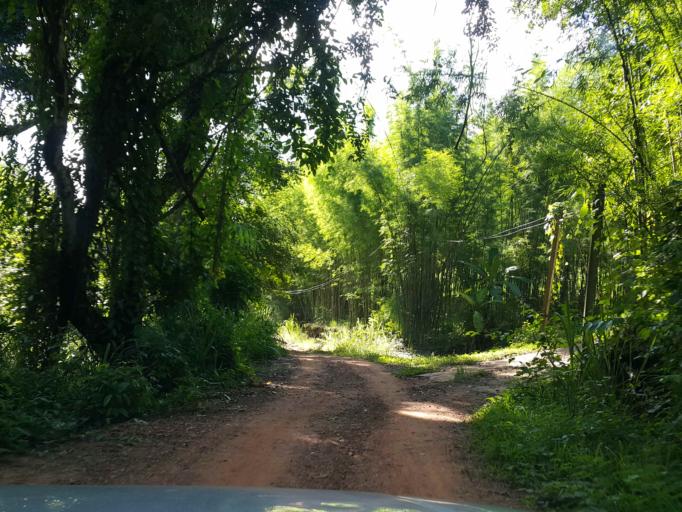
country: TH
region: Chiang Mai
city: Mae Taeng
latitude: 18.9731
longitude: 98.8906
